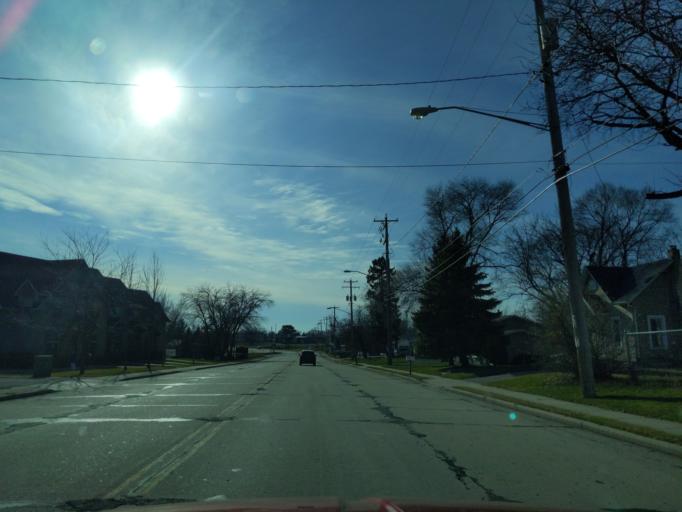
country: US
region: Wisconsin
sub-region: Walworth County
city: Whitewater
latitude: 42.8259
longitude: -88.7440
